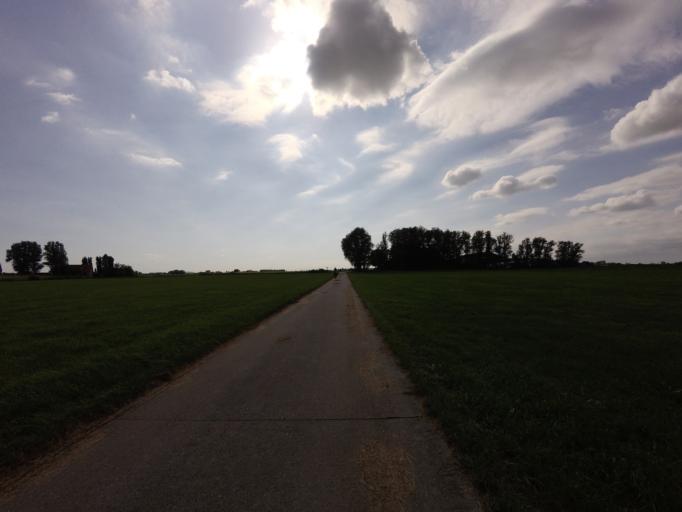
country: NL
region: Friesland
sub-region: Gemeente Littenseradiel
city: Makkum
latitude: 53.0866
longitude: 5.6325
